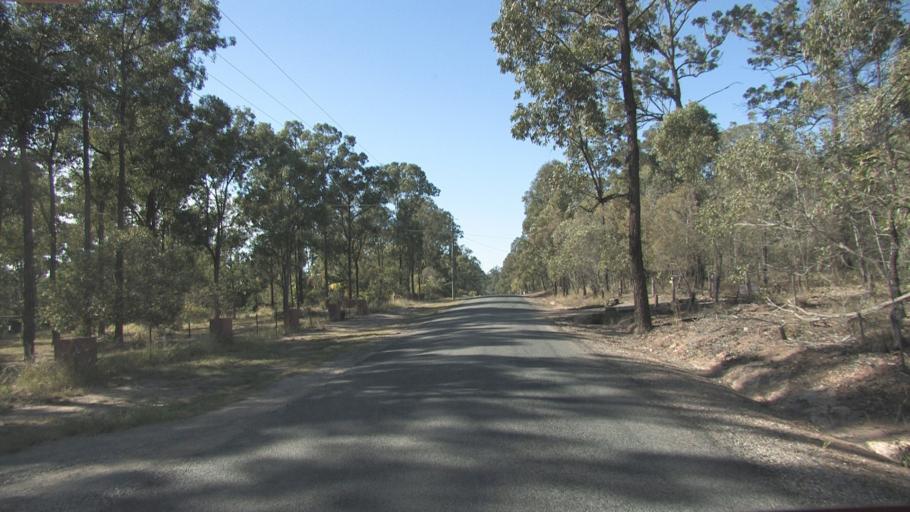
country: AU
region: Queensland
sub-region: Ipswich
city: Springfield Lakes
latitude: -27.6993
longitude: 152.9430
